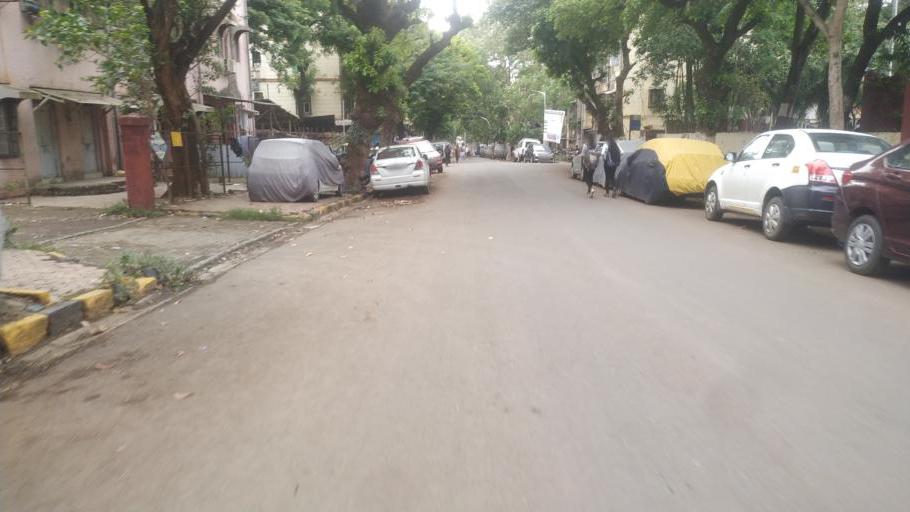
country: IN
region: Maharashtra
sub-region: Mumbai Suburban
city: Mumbai
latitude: 19.0093
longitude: 72.8465
